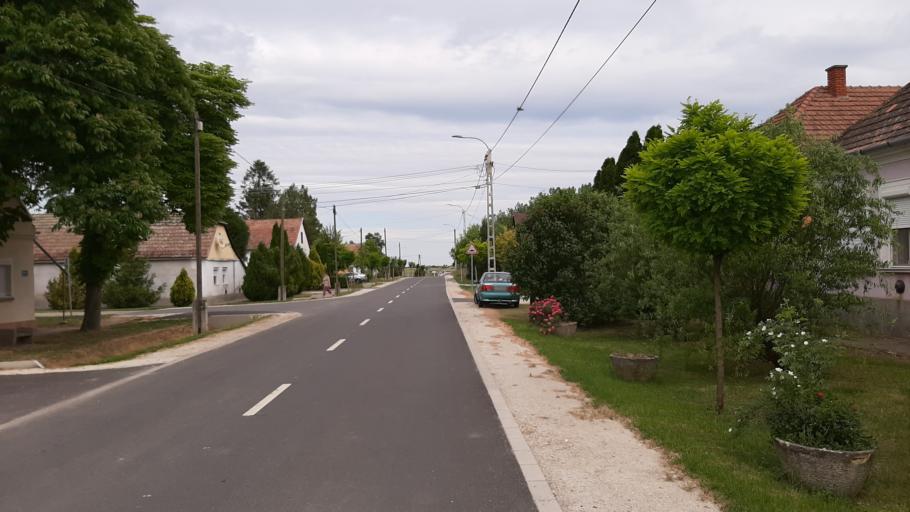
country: RO
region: Timis
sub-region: Comuna Beba Veche
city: Beba Veche
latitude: 46.1441
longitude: 20.2765
